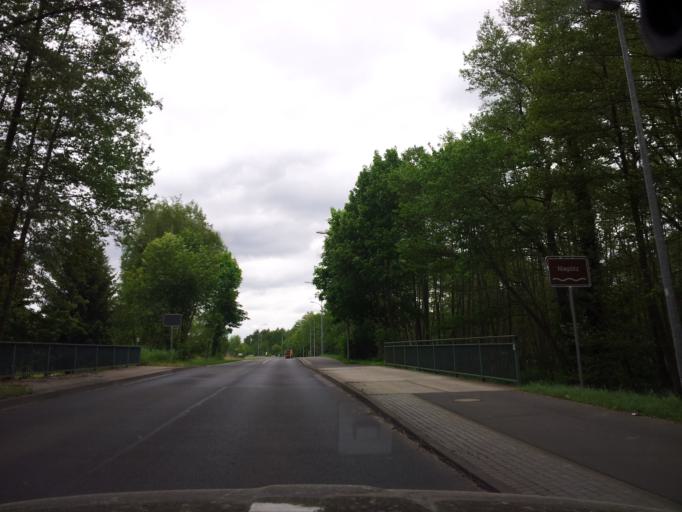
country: DE
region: Brandenburg
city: Treuenbrietzen
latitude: 52.0924
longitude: 12.8659
